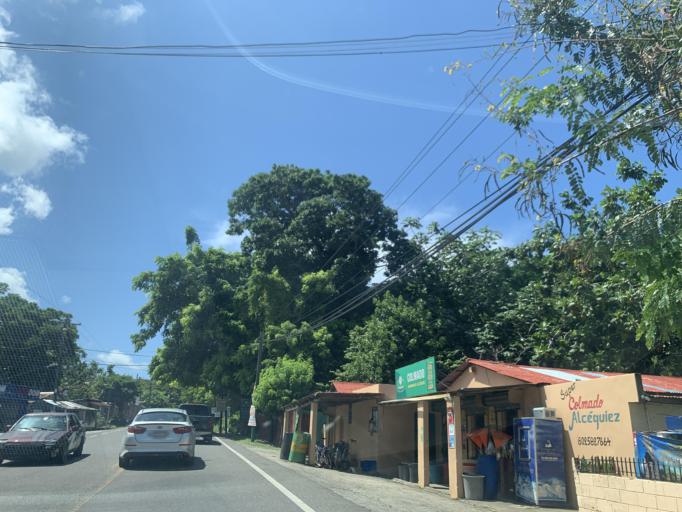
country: DO
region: Maria Trinidad Sanchez
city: Cabrera
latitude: 19.6507
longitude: -69.9310
